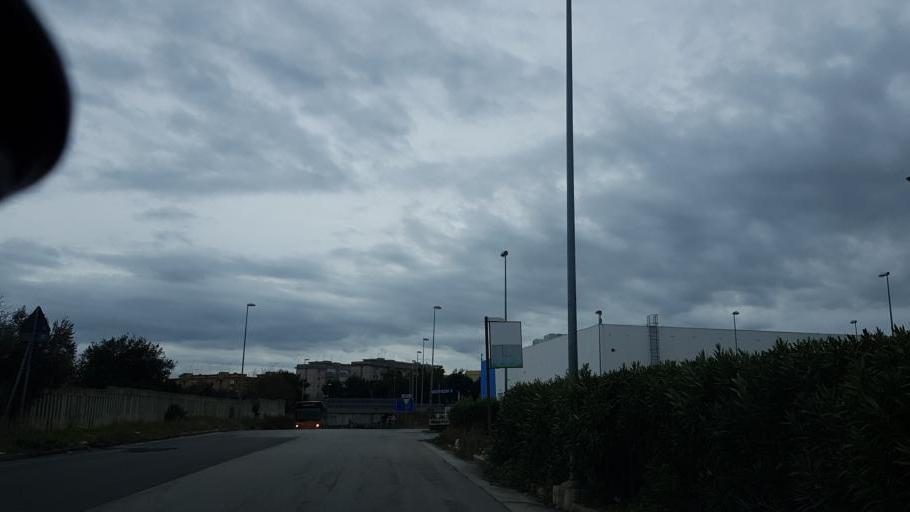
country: IT
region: Apulia
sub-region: Provincia di Brindisi
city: Brindisi
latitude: 40.6236
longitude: 17.9106
